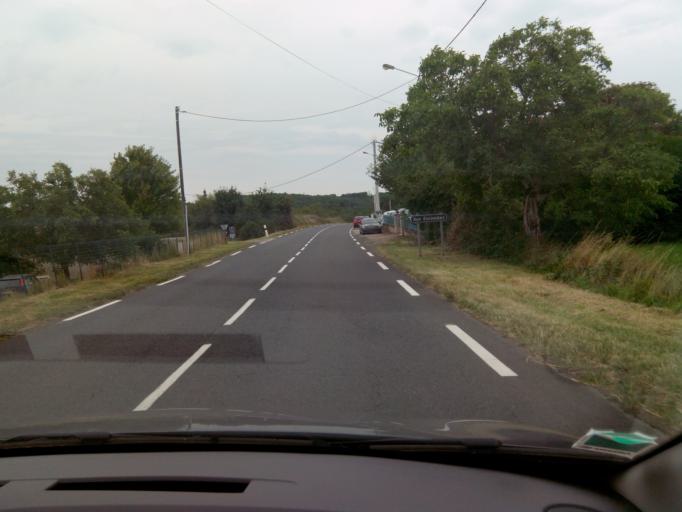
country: FR
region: Limousin
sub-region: Departement de la Correze
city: Cosnac
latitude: 45.0783
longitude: 1.5603
